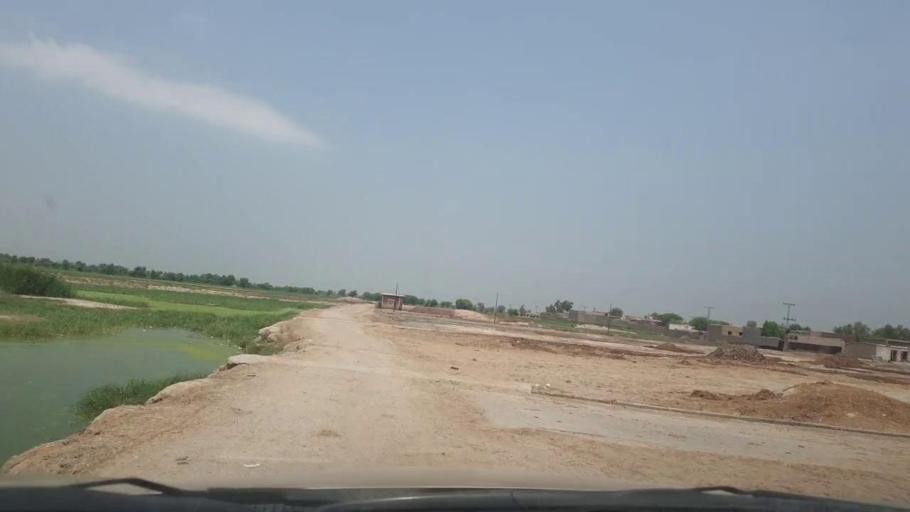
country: PK
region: Sindh
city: Ratodero
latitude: 27.7260
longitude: 68.2953
